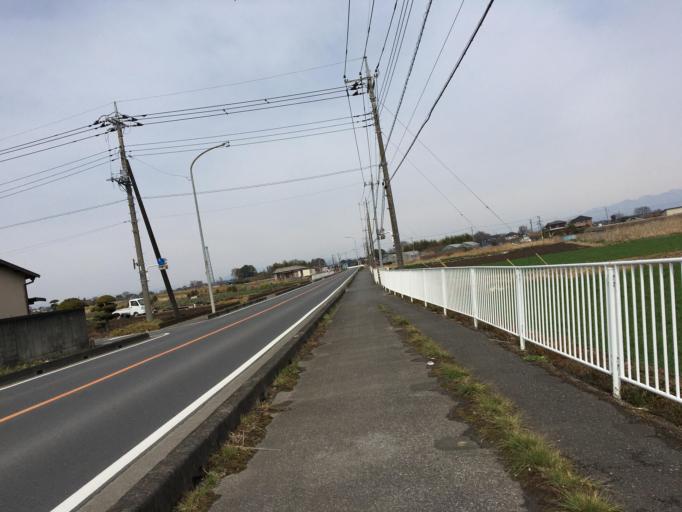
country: JP
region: Saitama
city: Yorii
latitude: 36.1404
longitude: 139.2118
